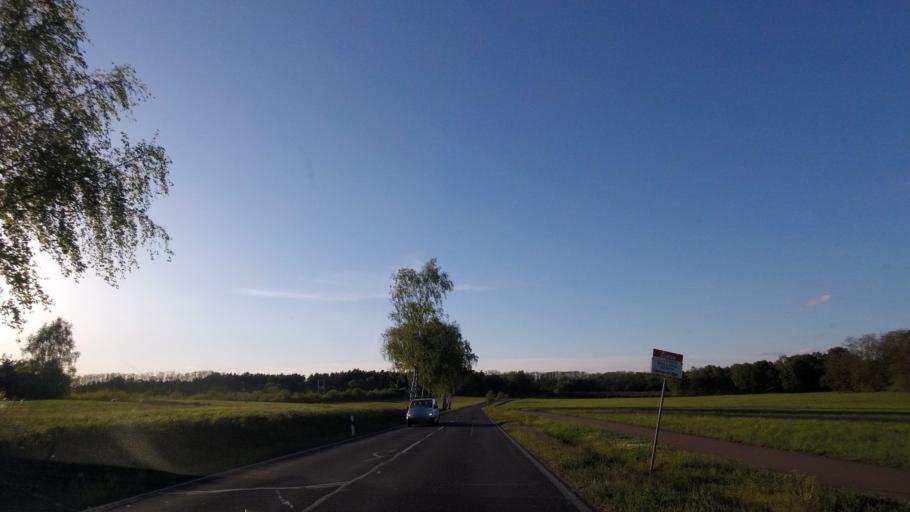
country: DE
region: Brandenburg
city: Juterbog
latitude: 52.0065
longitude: 13.0737
